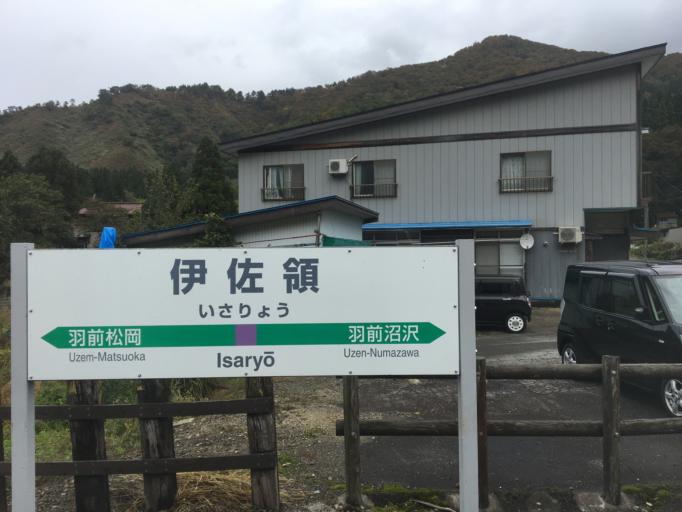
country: JP
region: Yamagata
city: Nagai
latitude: 38.0509
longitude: 139.8227
